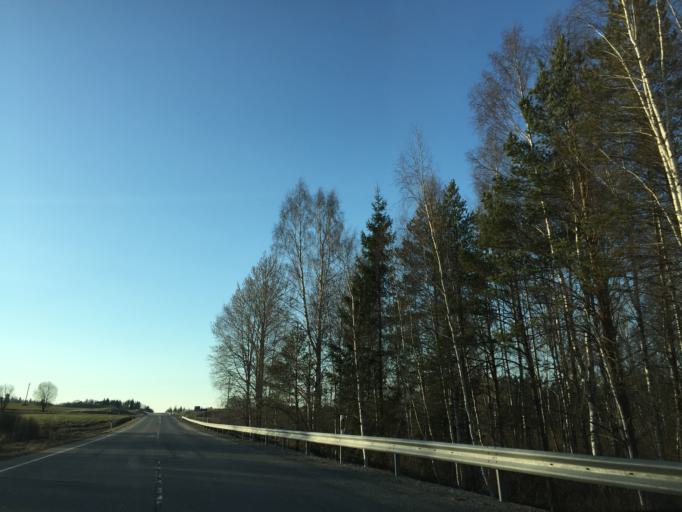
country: EE
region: Ida-Virumaa
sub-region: Johvi vald
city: Johvi
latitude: 59.1913
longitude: 27.5570
